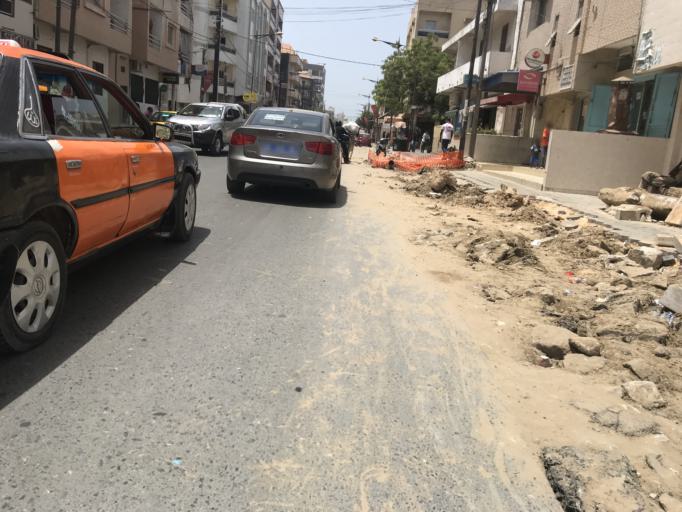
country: SN
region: Dakar
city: Dakar
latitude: 14.6791
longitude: -17.4541
